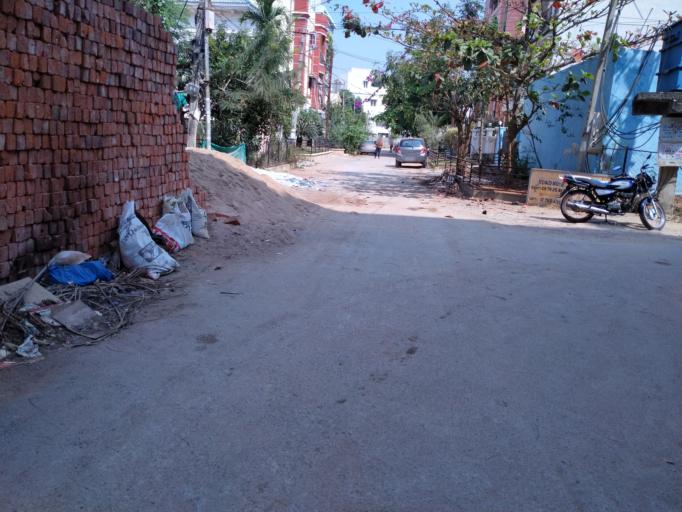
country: IN
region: Telangana
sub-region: Rangareddi
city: Secunderabad
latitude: 17.4950
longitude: 78.5475
